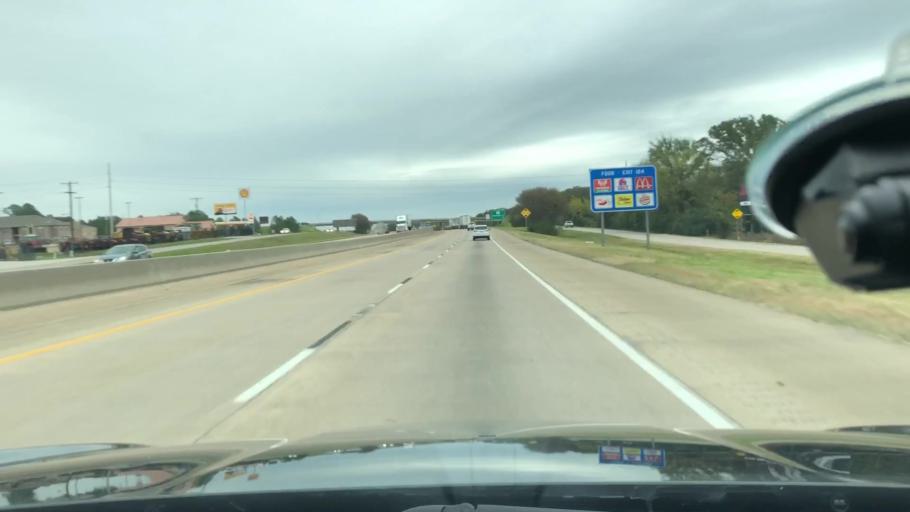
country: US
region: Texas
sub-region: Hopkins County
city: Sulphur Springs
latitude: 33.1169
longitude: -95.6176
